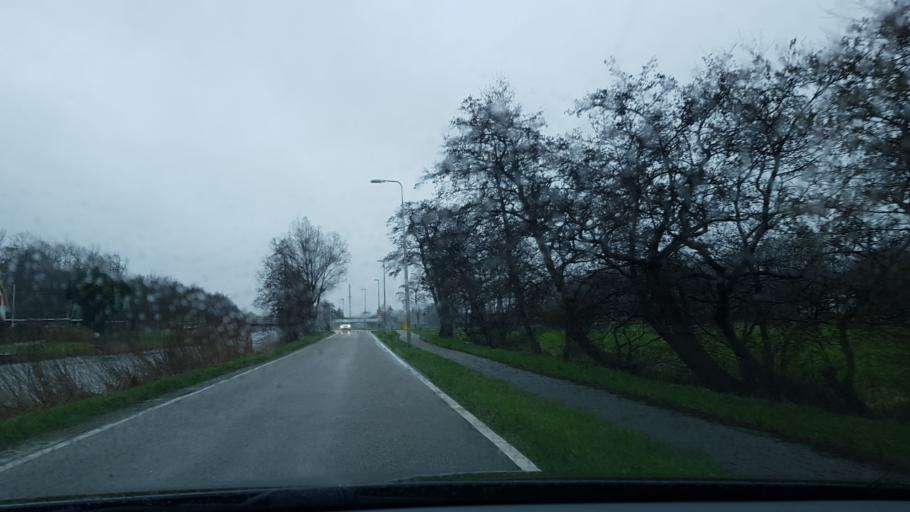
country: NL
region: North Holland
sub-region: Gemeente Bloemendaal
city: Bennebroek
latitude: 52.3385
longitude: 4.5966
